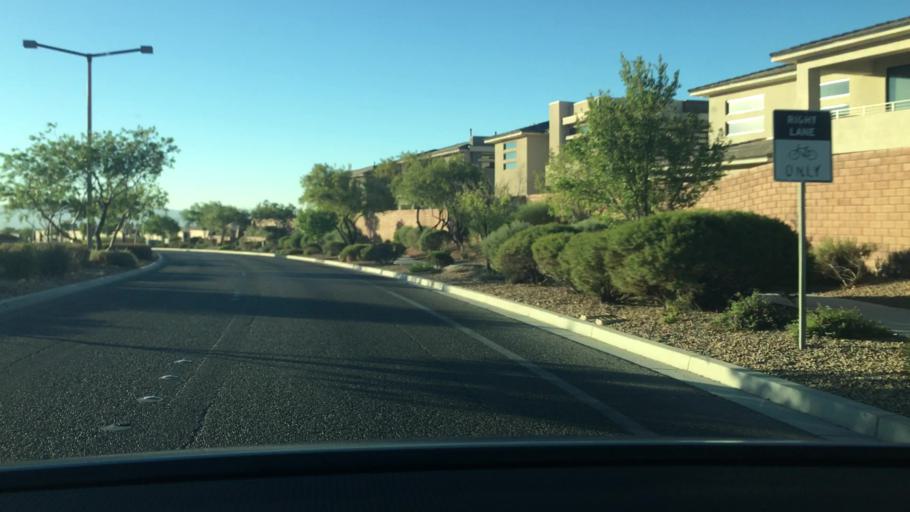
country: US
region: Nevada
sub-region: Clark County
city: Summerlin South
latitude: 36.1171
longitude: -115.3346
